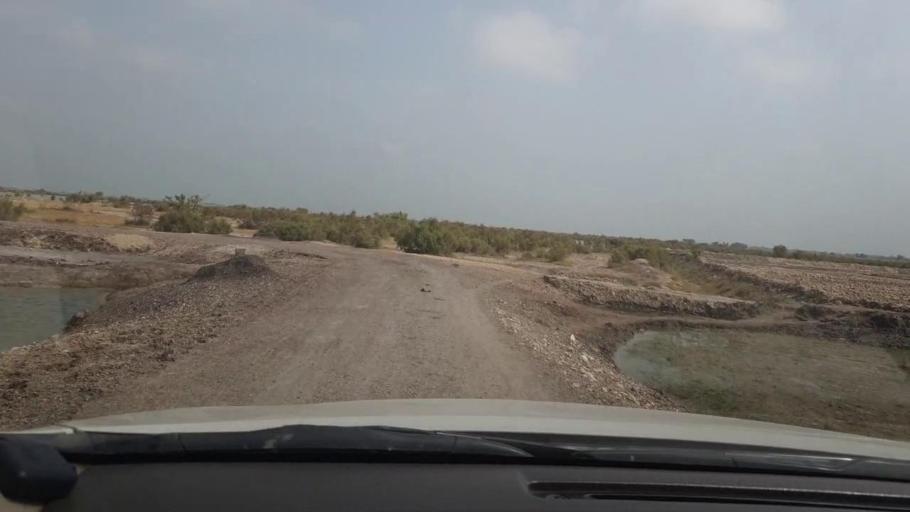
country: PK
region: Sindh
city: Shikarpur
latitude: 28.0250
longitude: 68.5899
